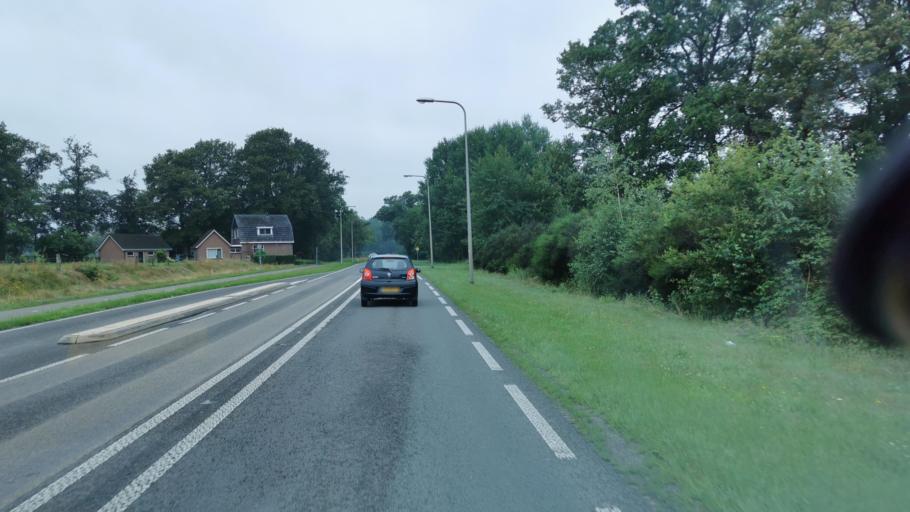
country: NL
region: Overijssel
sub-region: Gemeente Oldenzaal
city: Oldenzaal
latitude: 52.2861
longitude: 6.9526
